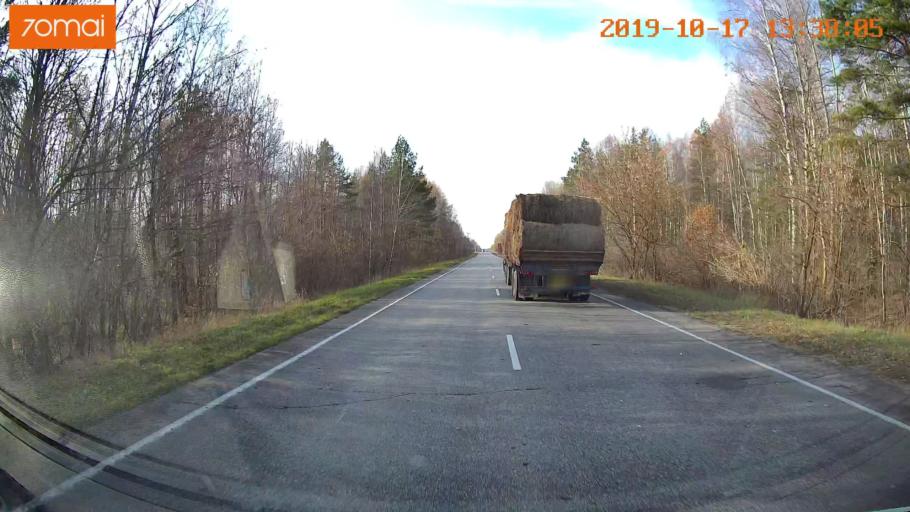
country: RU
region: Rjazan
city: Tuma
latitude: 55.1430
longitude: 40.6227
